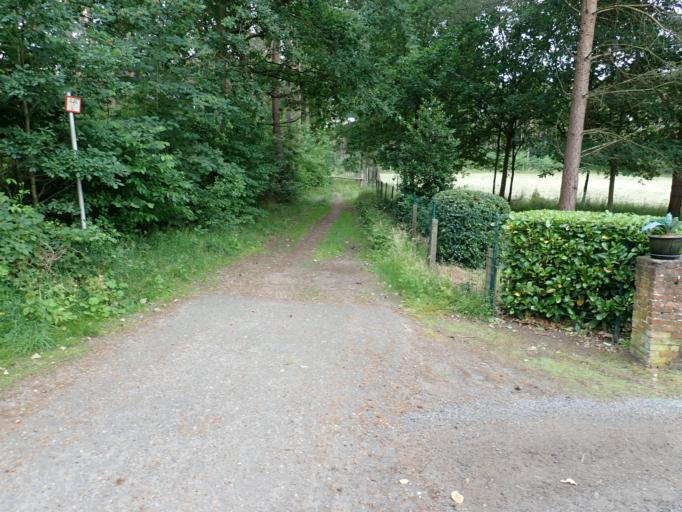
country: BE
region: Flanders
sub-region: Provincie Antwerpen
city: Bonheiden
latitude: 51.0203
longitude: 4.5866
